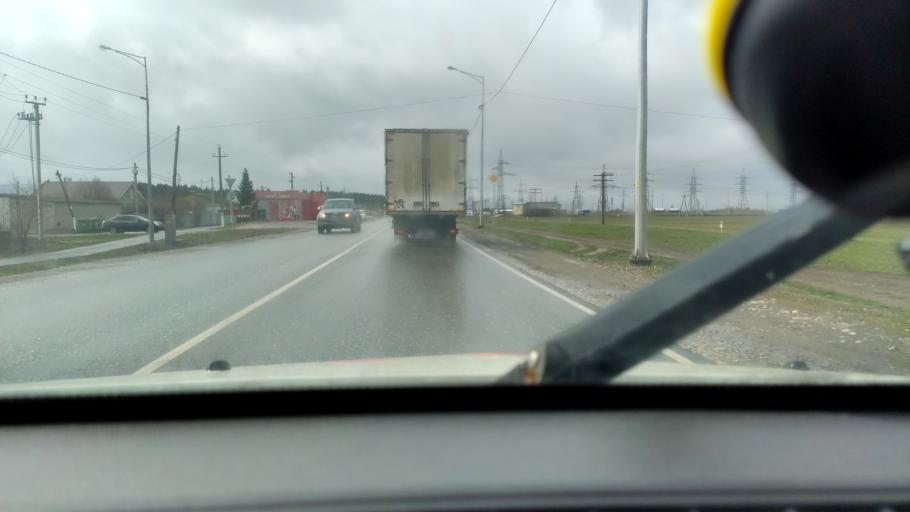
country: RU
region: Samara
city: Zhigulevsk
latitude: 53.5453
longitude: 49.5183
